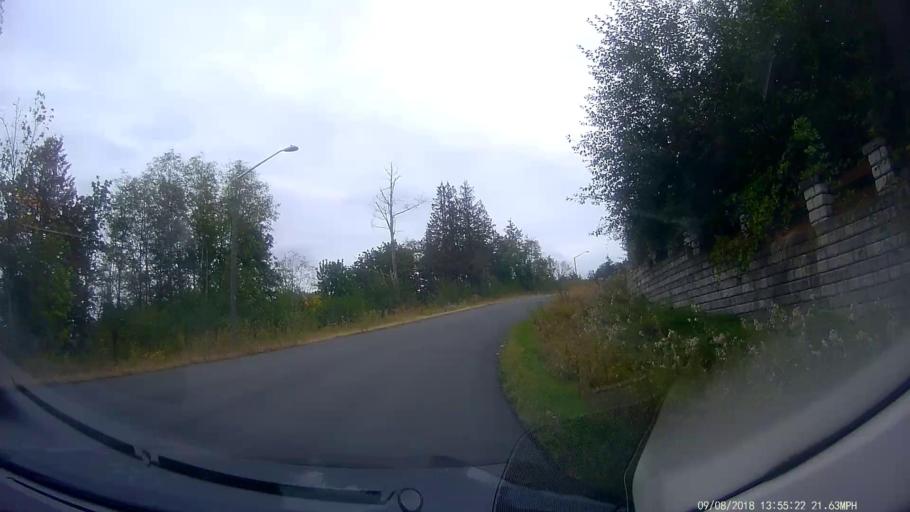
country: US
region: Washington
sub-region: Skagit County
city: Anacortes
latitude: 48.4623
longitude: -122.5841
